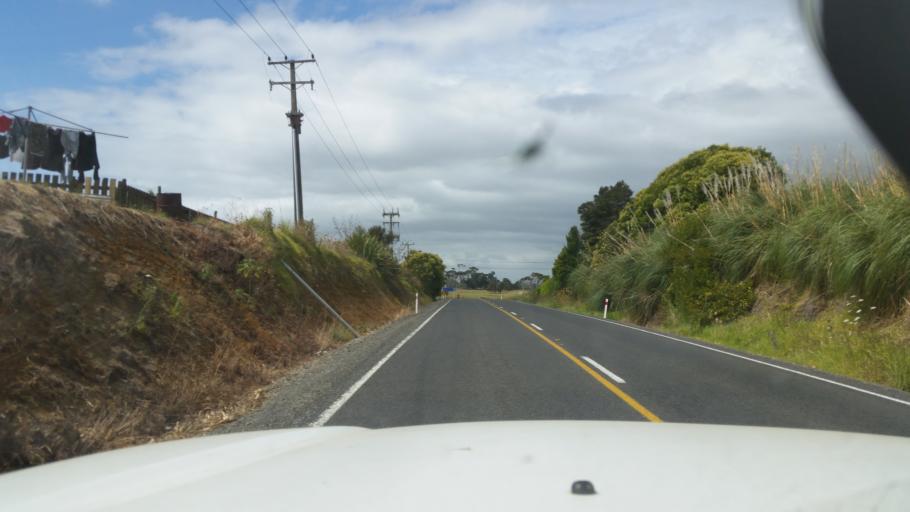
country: NZ
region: Northland
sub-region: Far North District
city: Ahipara
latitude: -35.1733
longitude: 173.1793
